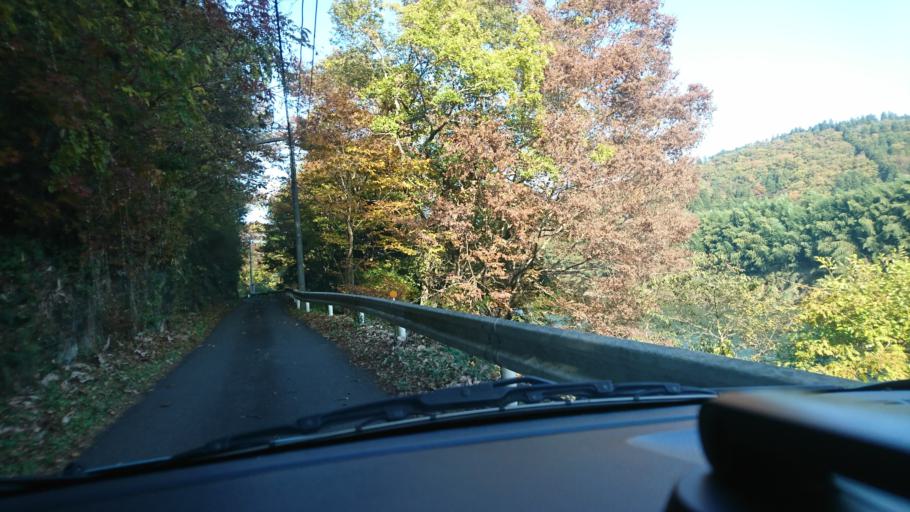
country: JP
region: Iwate
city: Ichinoseki
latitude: 38.7990
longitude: 141.2465
